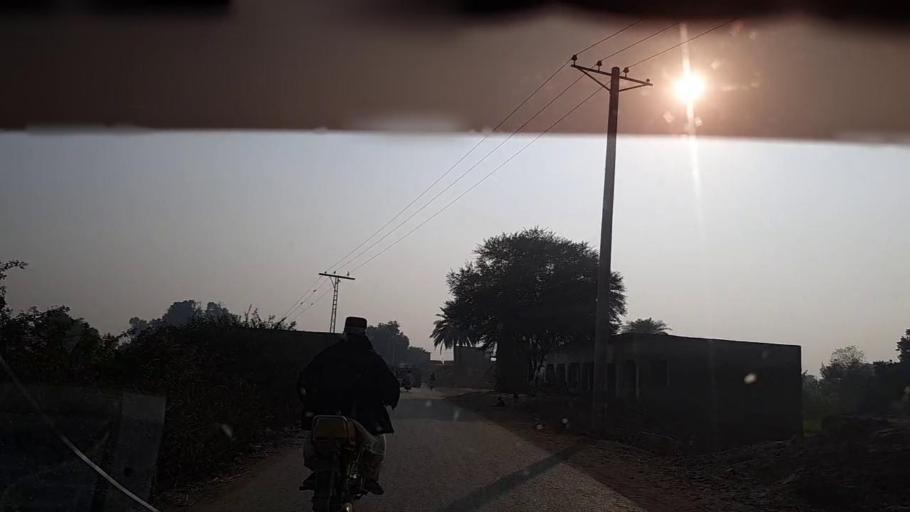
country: PK
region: Sindh
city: Sobhadero
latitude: 27.4431
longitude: 68.3906
